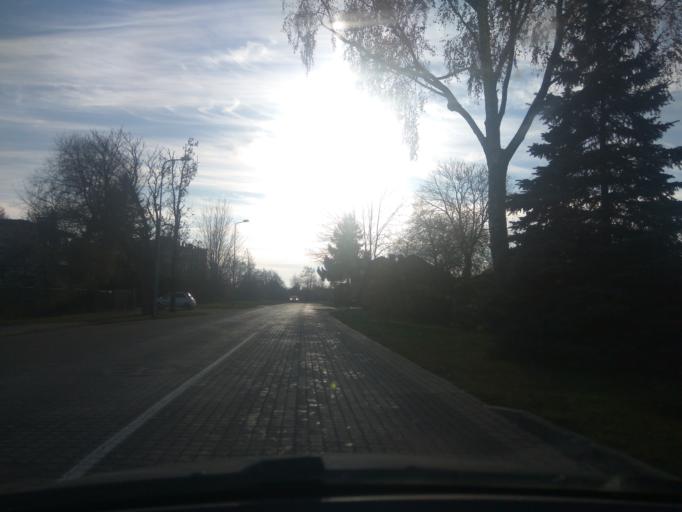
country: LV
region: Ventspils
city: Ventspils
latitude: 57.3720
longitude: 21.5697
